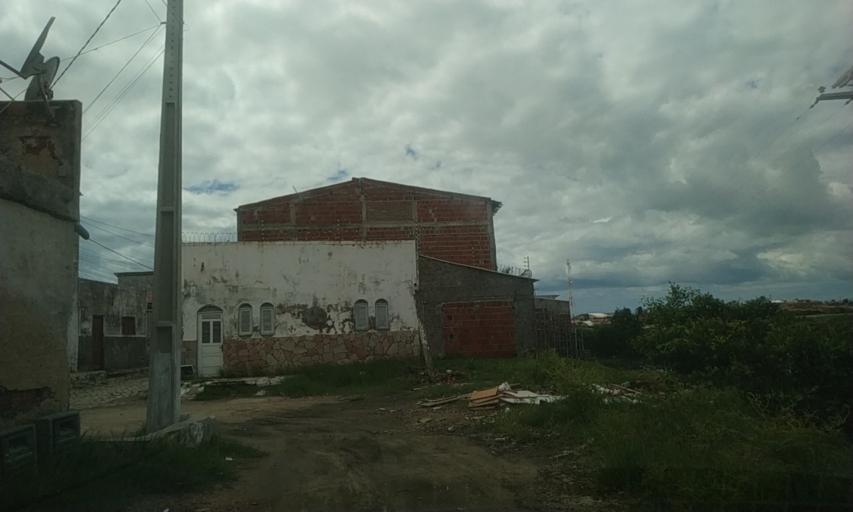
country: BR
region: Rio Grande do Norte
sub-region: Areia Branca
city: Areia Branca
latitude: -4.9568
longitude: -37.1306
